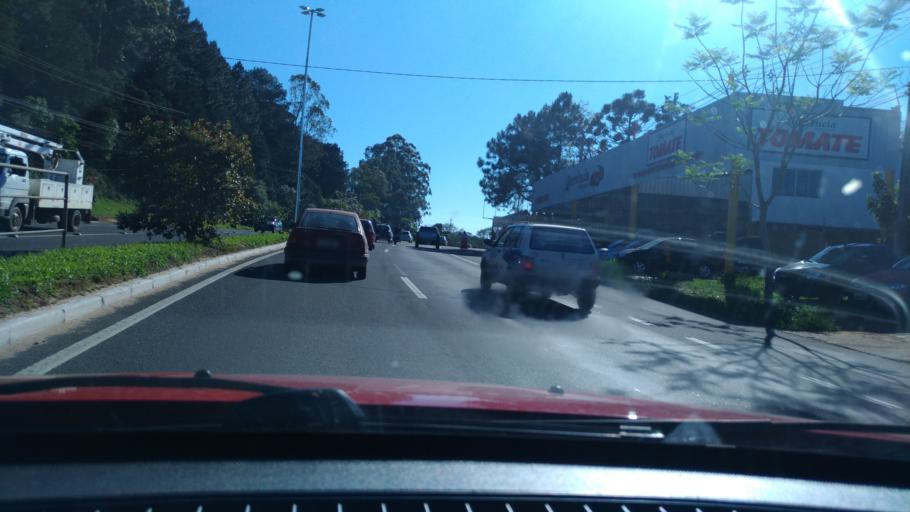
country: BR
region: Rio Grande do Sul
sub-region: Viamao
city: Viamao
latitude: -30.0771
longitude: -51.0488
